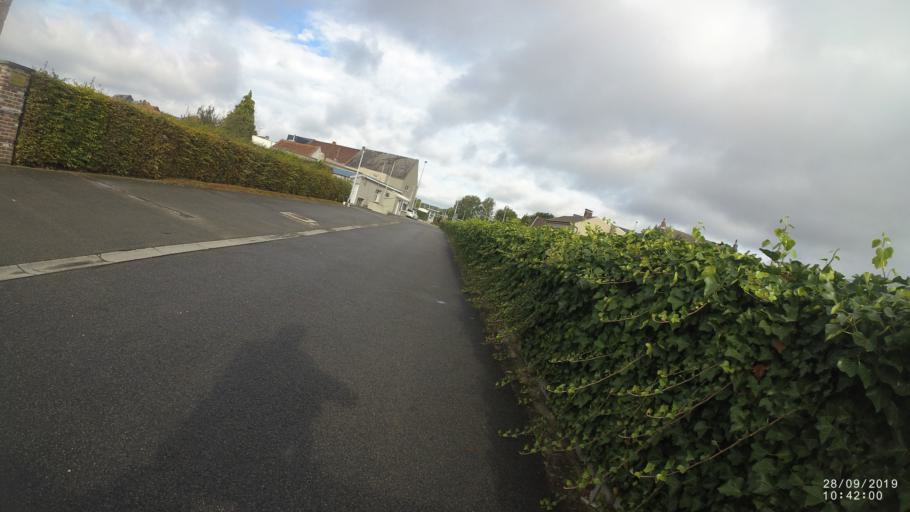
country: BE
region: Flanders
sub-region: Provincie Oost-Vlaanderen
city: Sint-Maria-Lierde
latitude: 50.8150
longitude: 3.8283
